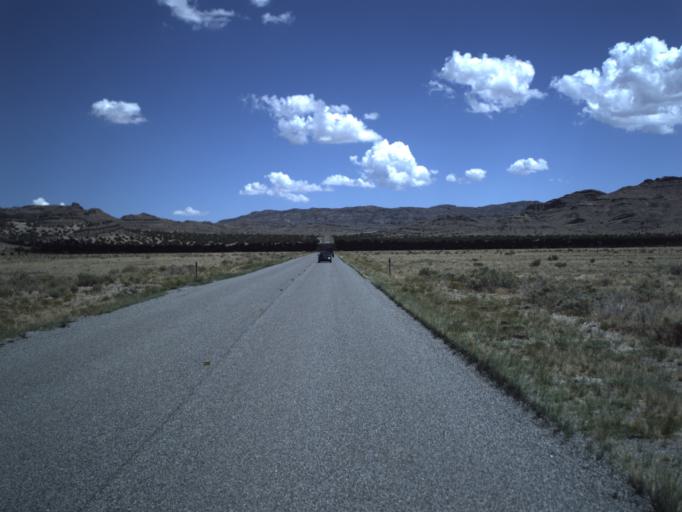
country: US
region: Utah
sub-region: Beaver County
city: Milford
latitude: 39.0677
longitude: -113.7355
